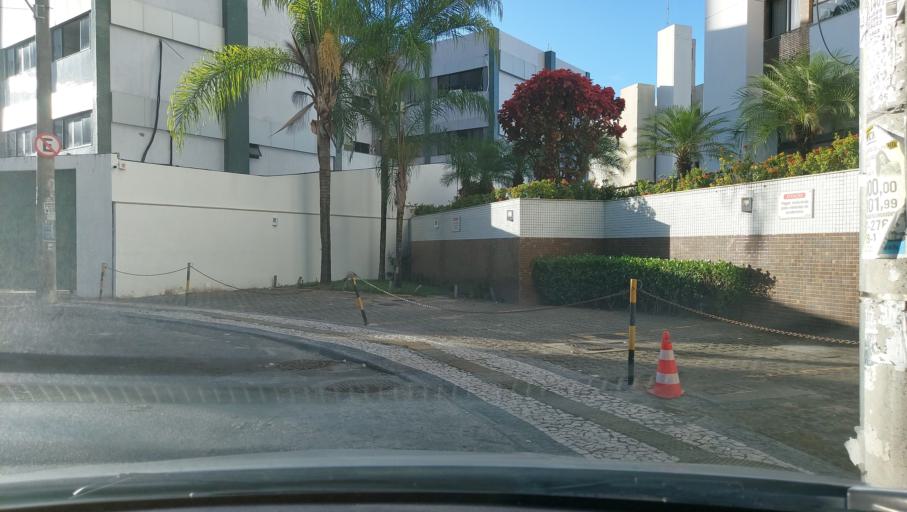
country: BR
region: Bahia
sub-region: Salvador
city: Salvador
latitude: -12.9716
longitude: -38.4379
